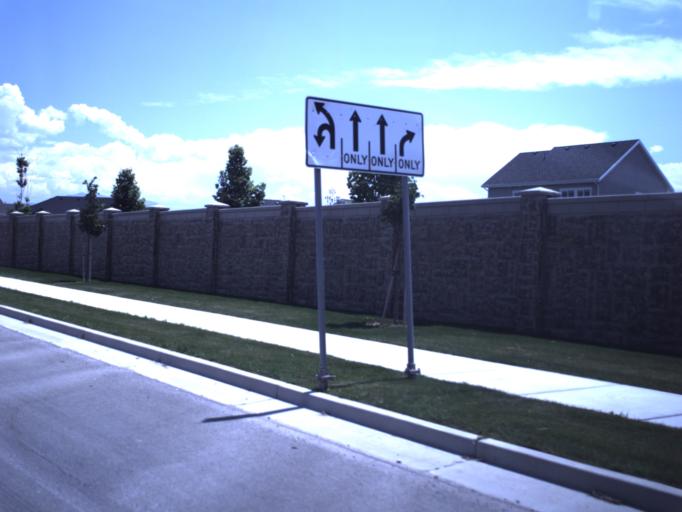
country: US
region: Utah
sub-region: Utah County
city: Lehi
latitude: 40.4124
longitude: -111.8890
